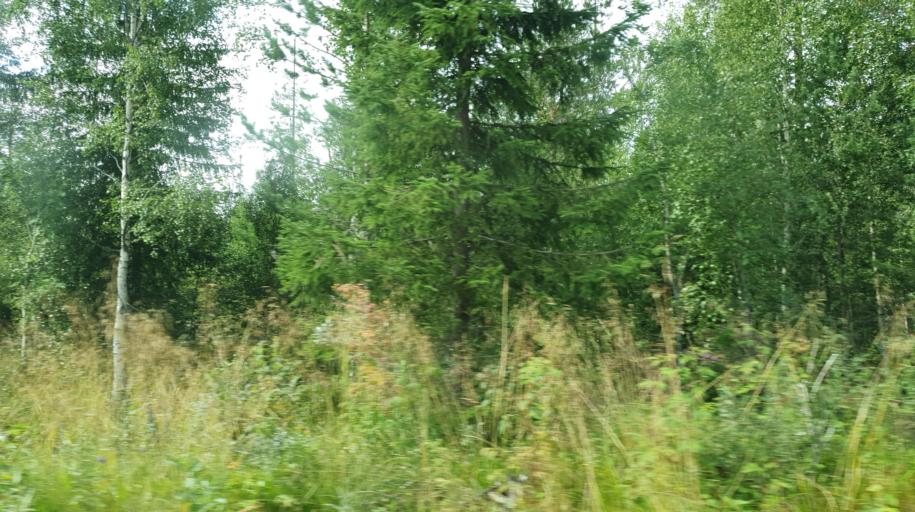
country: NO
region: Nord-Trondelag
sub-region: Levanger
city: Skogn
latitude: 63.5781
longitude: 11.2418
